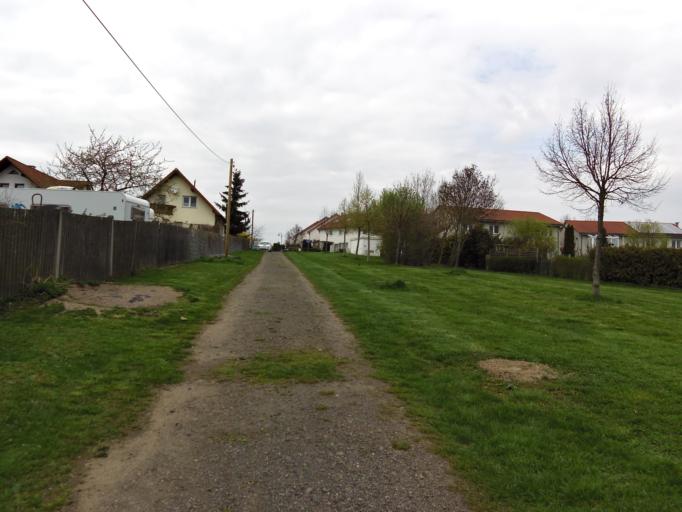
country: DE
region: Thuringia
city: Gotha
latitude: 50.9489
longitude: 10.6730
